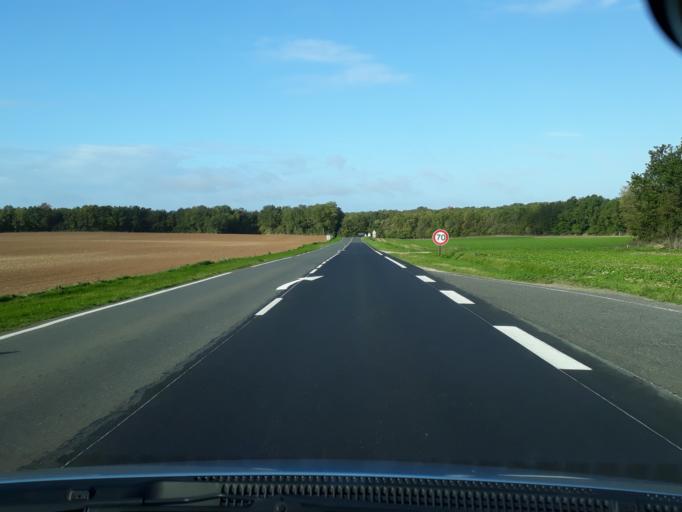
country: FR
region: Centre
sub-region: Departement du Loiret
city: Malesherbes
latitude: 48.3073
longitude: 2.4482
